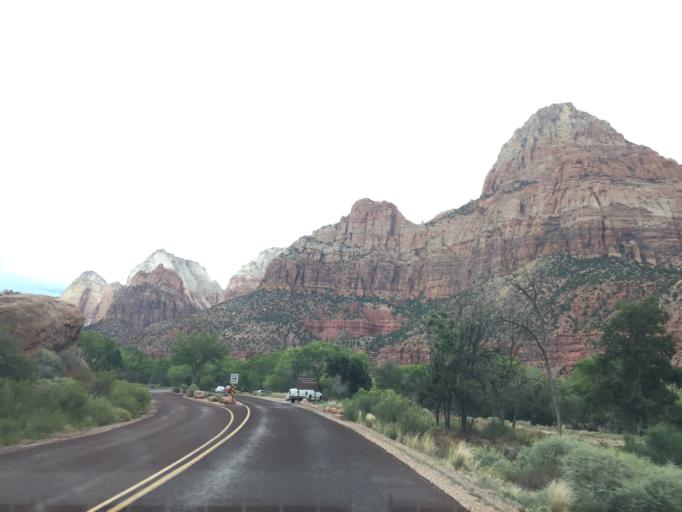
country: US
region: Utah
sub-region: Washington County
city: Hildale
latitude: 37.2041
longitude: -112.9853
